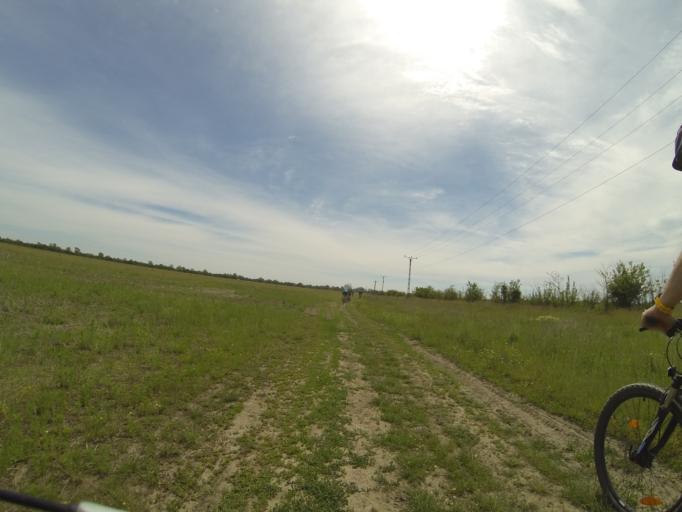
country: RO
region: Dolj
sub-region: Comuna Leu
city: Leu
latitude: 44.2019
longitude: 23.9735
